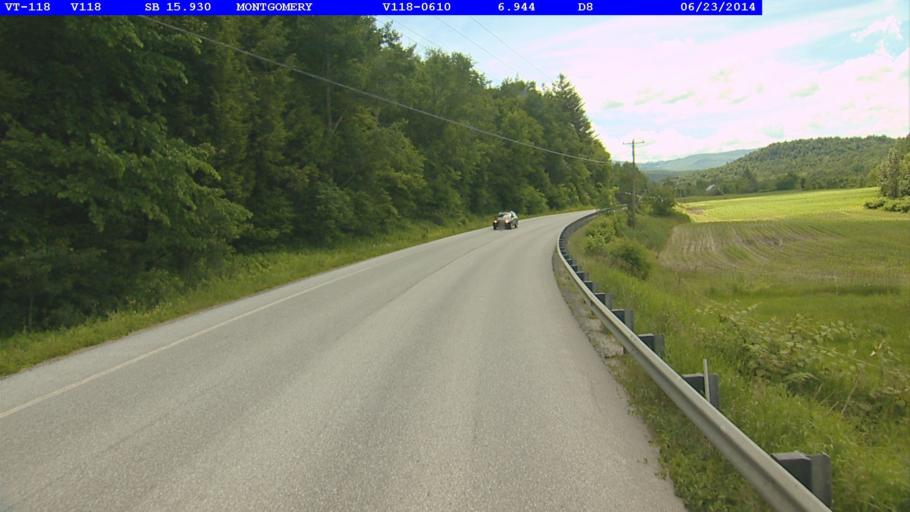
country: US
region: Vermont
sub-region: Franklin County
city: Richford
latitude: 44.8931
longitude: -72.6224
